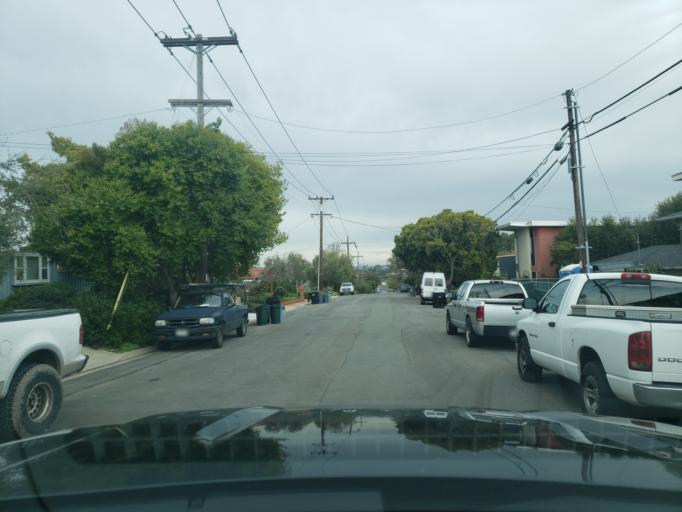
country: US
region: California
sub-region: San Diego County
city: Coronado
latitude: 32.7197
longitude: -117.2424
